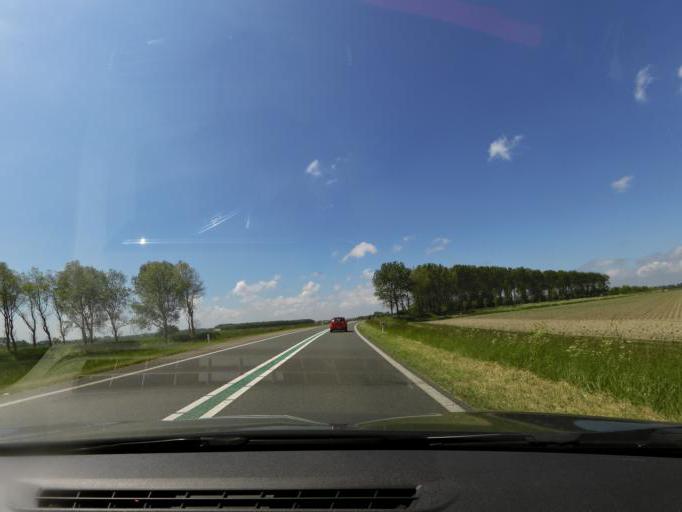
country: NL
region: Zeeland
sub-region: Gemeente Noord-Beveland
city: Kamperland
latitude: 51.5744
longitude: 3.7362
